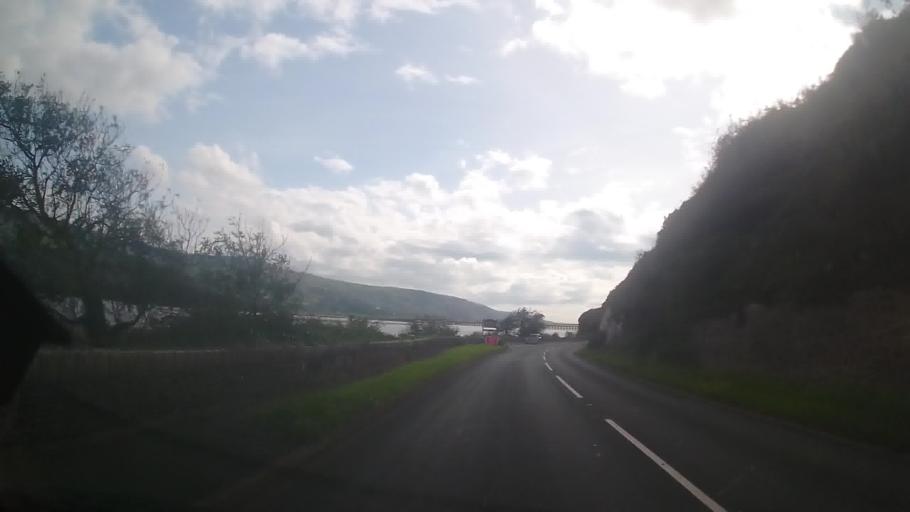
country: GB
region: Wales
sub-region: Gwynedd
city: Barmouth
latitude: 52.7245
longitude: -4.0325
